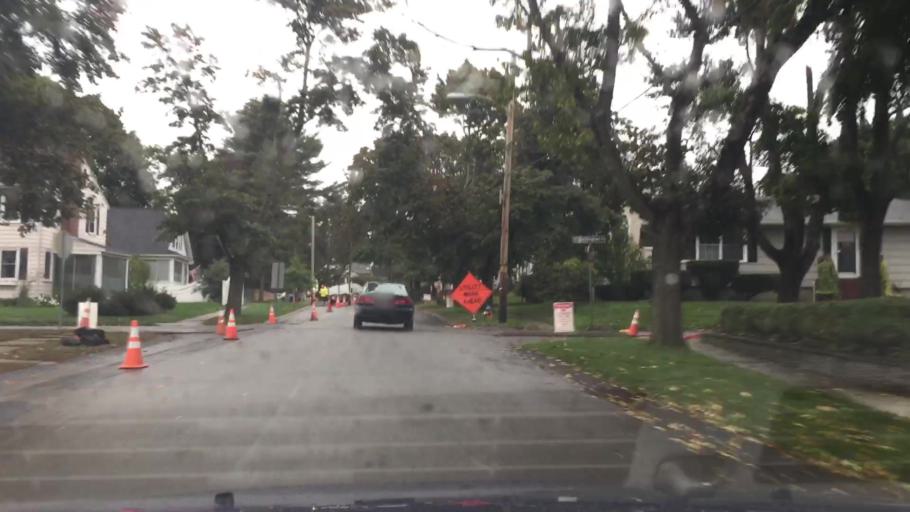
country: US
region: Massachusetts
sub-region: Essex County
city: North Andover
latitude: 42.6963
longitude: -71.1341
